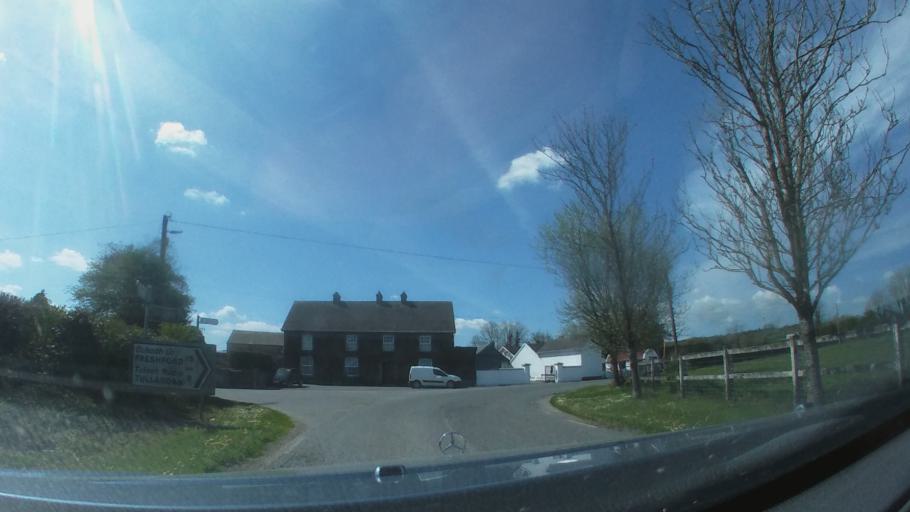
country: IE
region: Leinster
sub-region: Kilkenny
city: Callan
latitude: 52.6219
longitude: -7.4301
